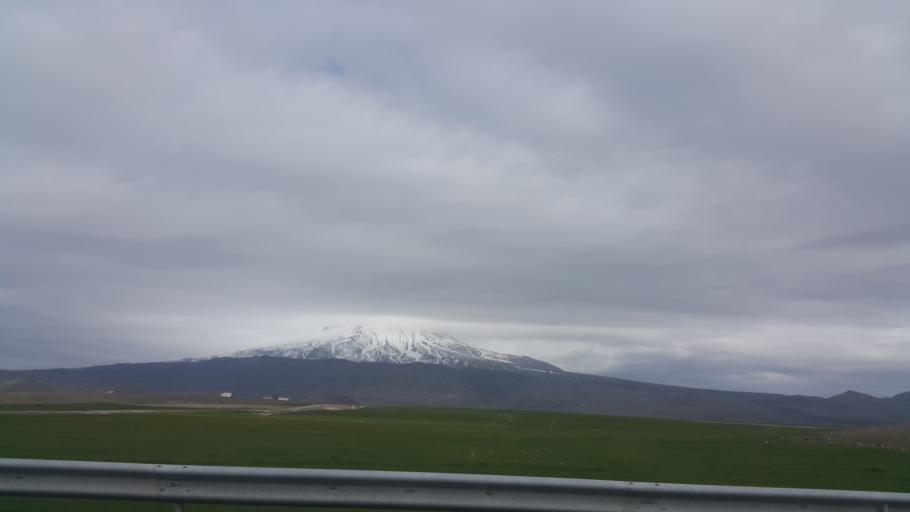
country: TR
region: Aksaray
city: Taspinar
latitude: 38.1221
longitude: 34.0341
